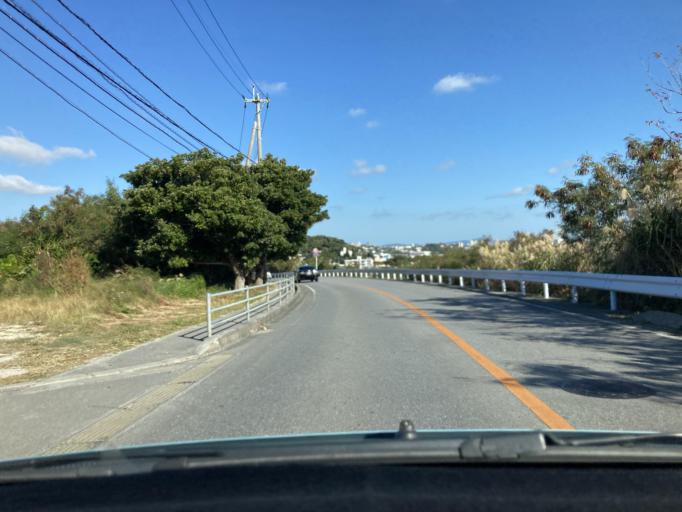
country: JP
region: Okinawa
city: Chatan
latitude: 26.2955
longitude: 127.7996
